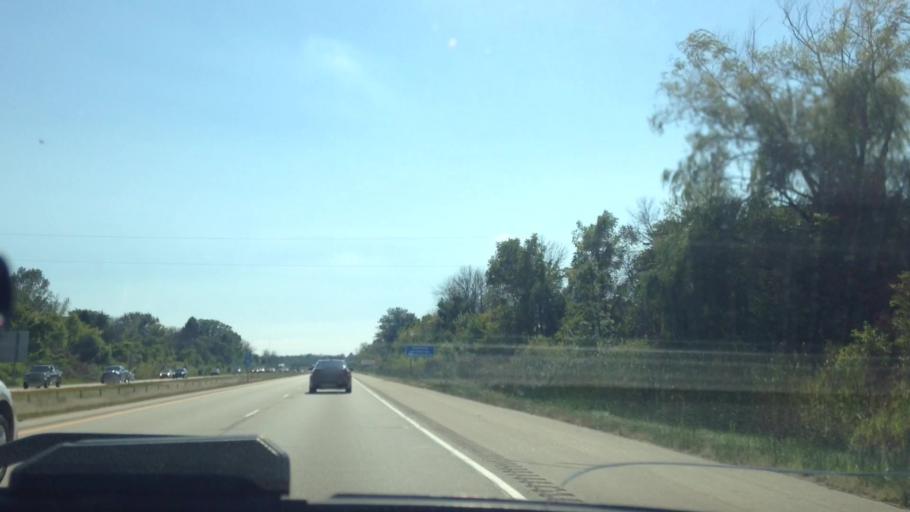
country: US
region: Wisconsin
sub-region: Milwaukee County
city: River Hills
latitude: 43.2046
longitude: -87.9222
